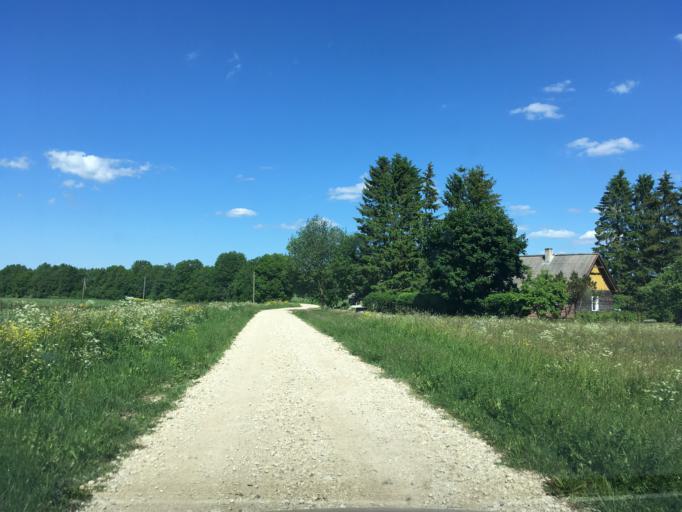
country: EE
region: Harju
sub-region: Anija vald
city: Kehra
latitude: 59.2590
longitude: 25.3032
